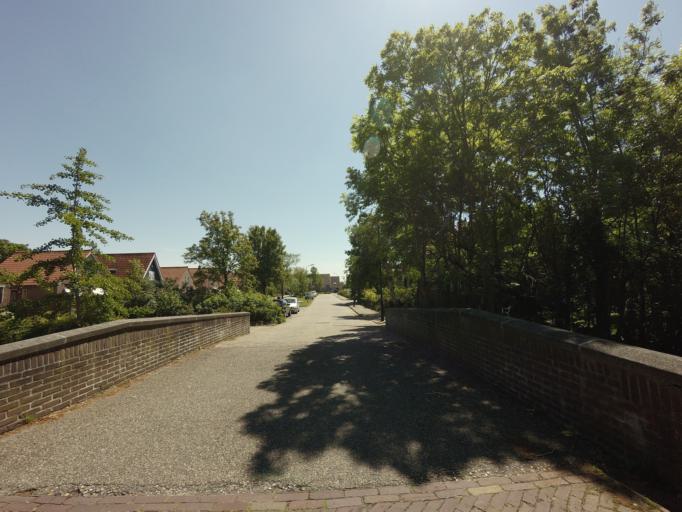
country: NL
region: North Holland
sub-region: Gemeente Uitgeest
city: Uitgeest
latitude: 52.5548
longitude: 4.7958
